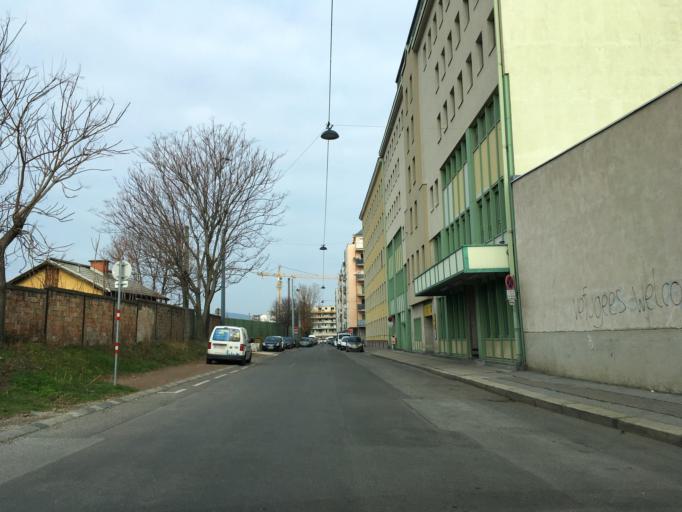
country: AT
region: Vienna
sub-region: Wien Stadt
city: Vienna
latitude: 48.2310
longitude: 16.3853
